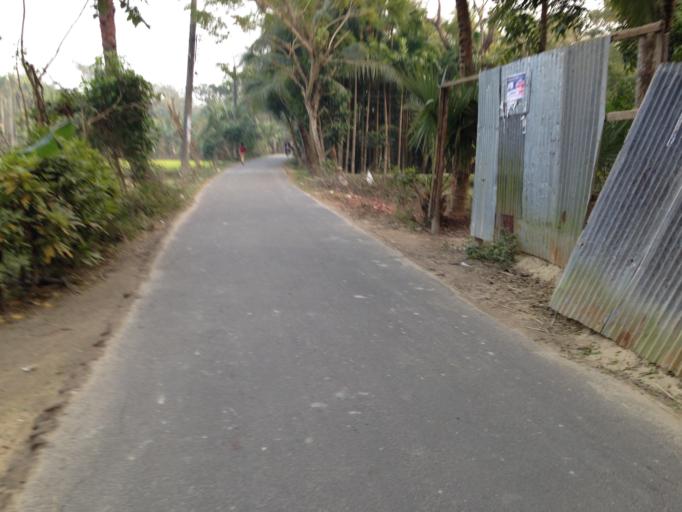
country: BD
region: Chittagong
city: Lakshmipur
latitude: 22.9194
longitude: 90.8405
